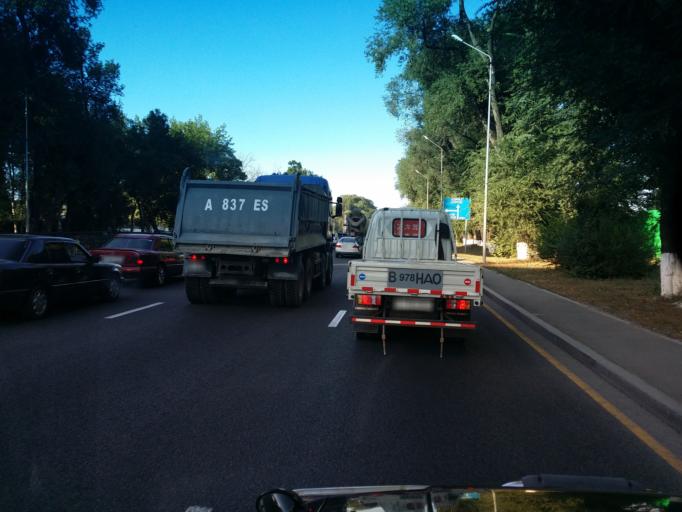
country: KZ
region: Almaty Qalasy
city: Almaty
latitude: 43.2939
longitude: 76.9954
